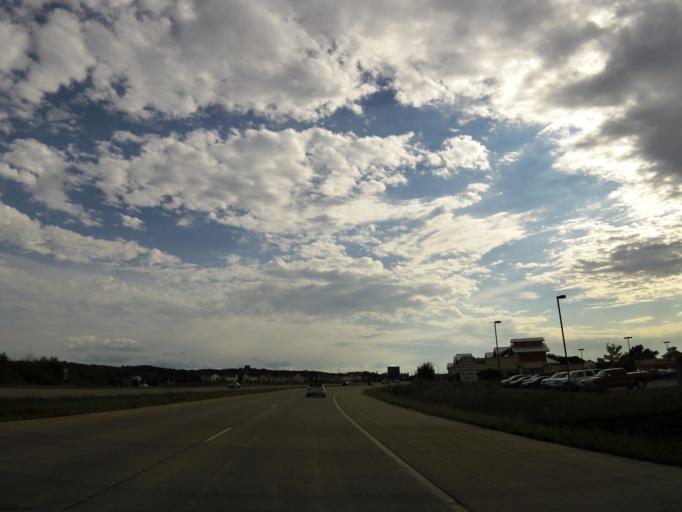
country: US
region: Minnesota
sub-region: Scott County
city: Prior Lake
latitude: 44.7766
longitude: -93.4131
